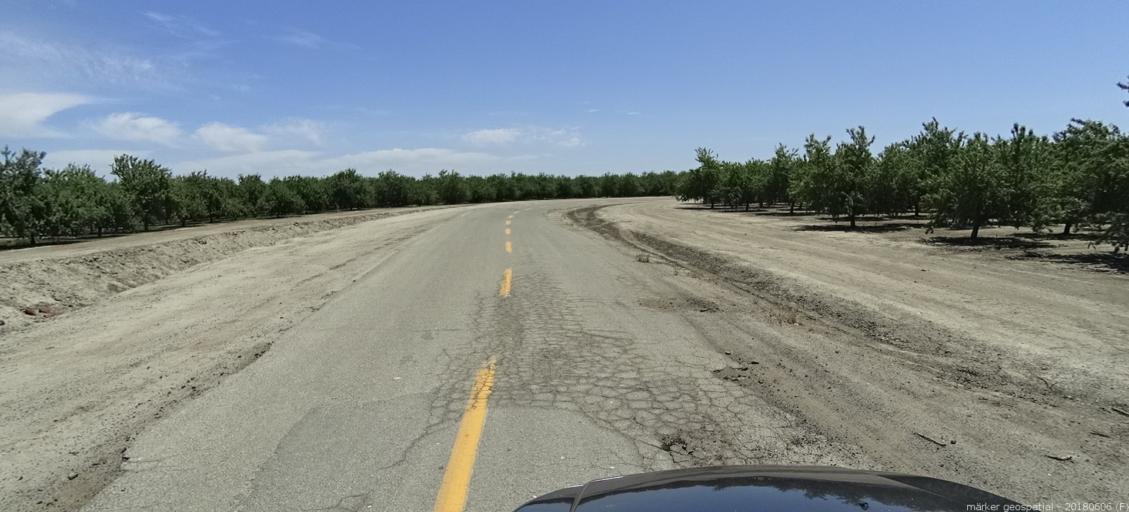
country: US
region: California
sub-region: Fresno County
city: Mendota
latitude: 36.8235
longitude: -120.3716
